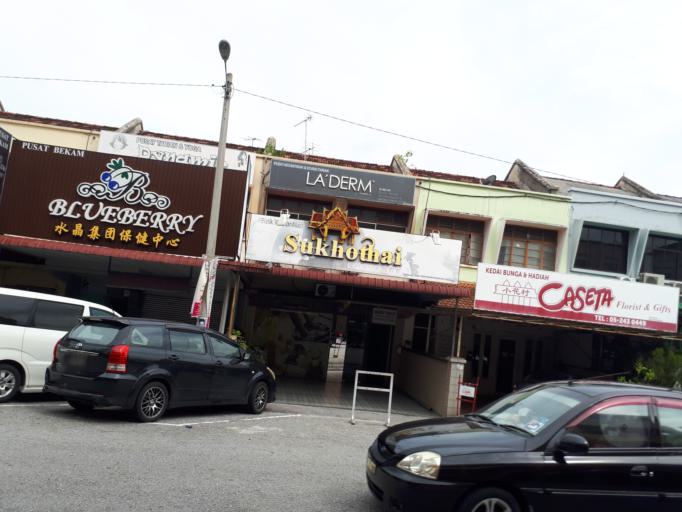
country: MY
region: Perak
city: Ipoh
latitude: 4.5991
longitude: 101.0872
